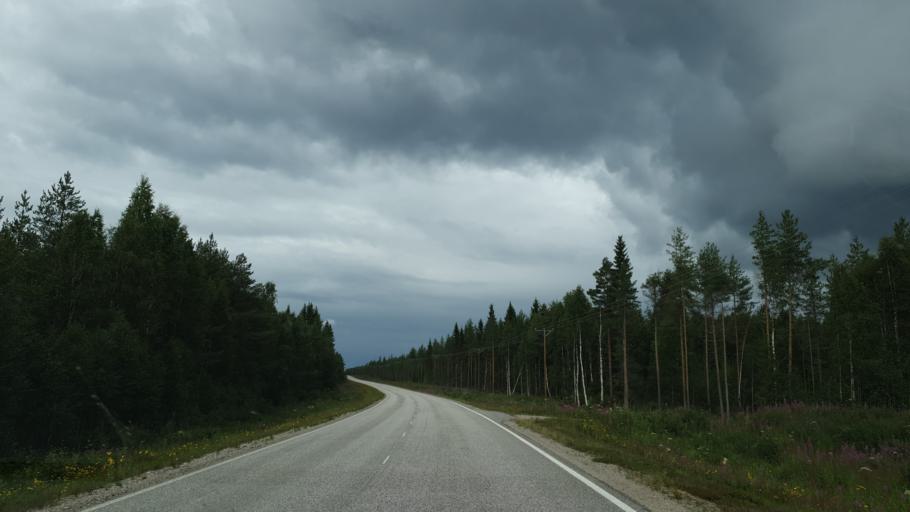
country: FI
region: Kainuu
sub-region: Kehys-Kainuu
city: Kuhmo
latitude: 64.3689
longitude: 29.8919
